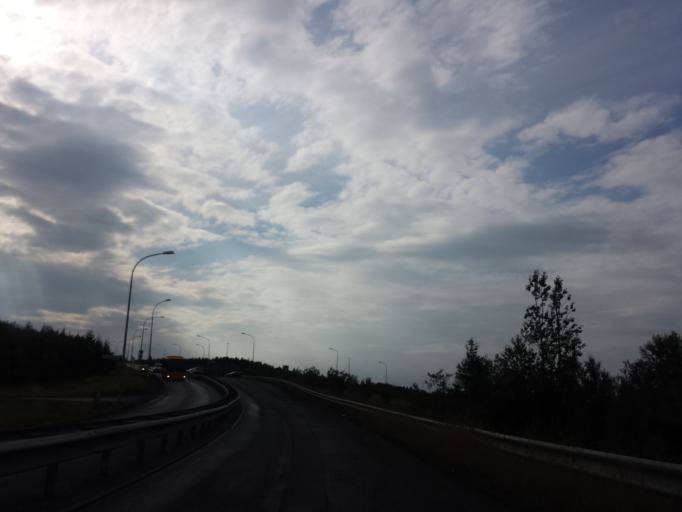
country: IS
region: Capital Region
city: Reykjavik
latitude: 64.1149
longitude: -21.8216
